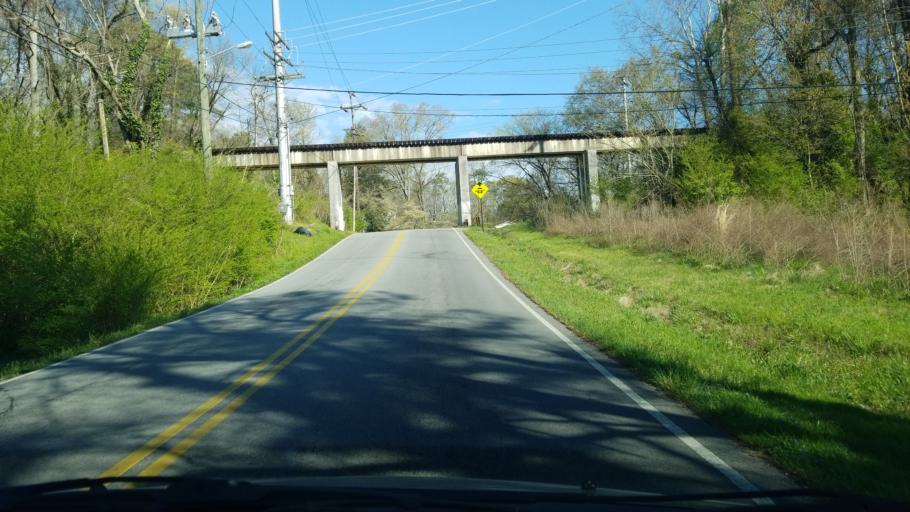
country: US
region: Tennessee
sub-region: Hamilton County
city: East Chattanooga
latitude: 35.0649
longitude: -85.2279
